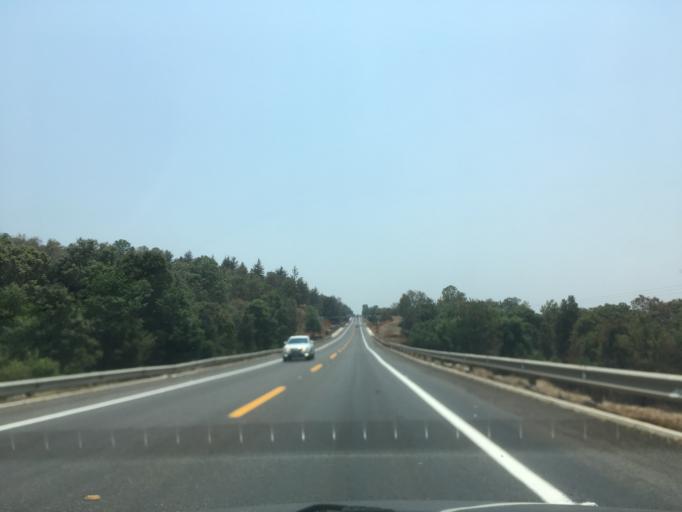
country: MX
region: Michoacan
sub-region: Patzcuaro
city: Santa Ana Chapitiro
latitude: 19.5070
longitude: -101.6717
